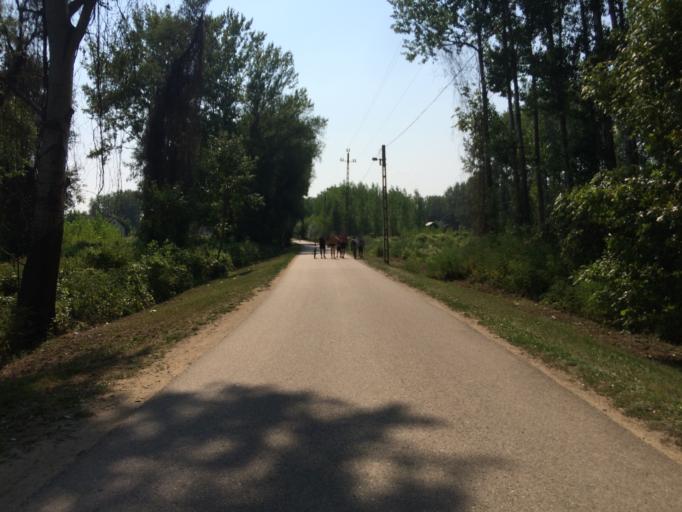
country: HU
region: Csongrad
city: Mindszent
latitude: 46.5231
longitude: 20.1699
